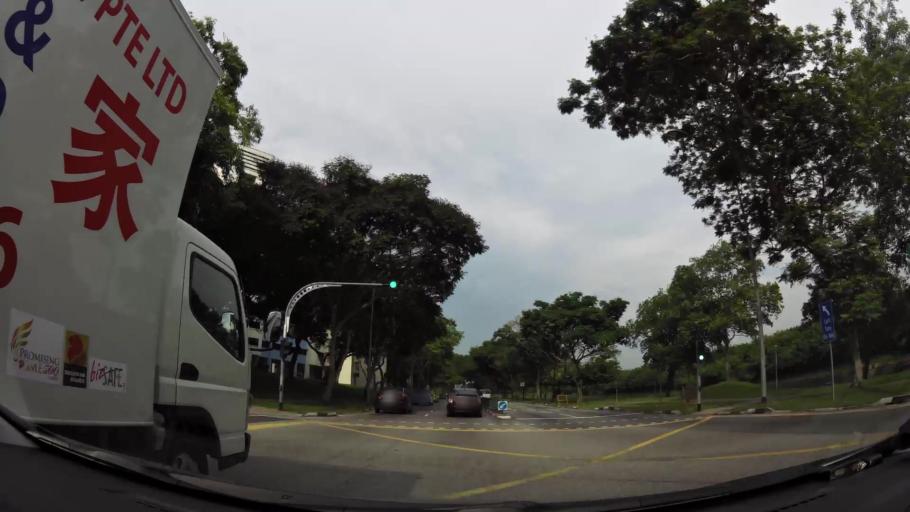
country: SG
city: Singapore
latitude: 1.3657
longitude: 103.8978
